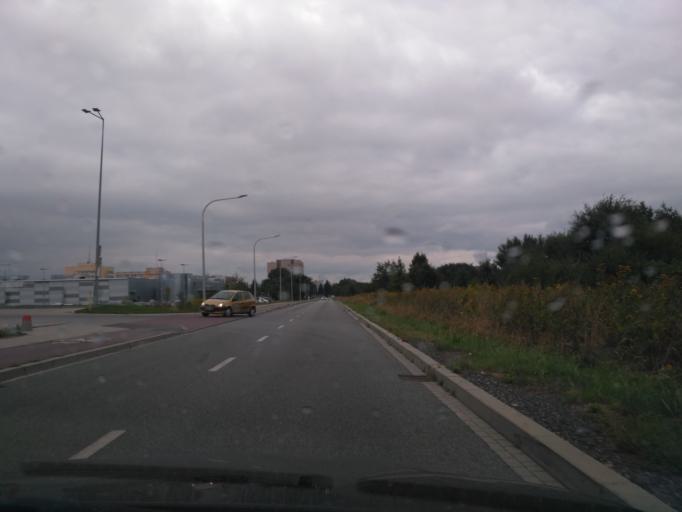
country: PL
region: Subcarpathian Voivodeship
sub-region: Krosno
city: Krosno
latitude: 49.6756
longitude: 21.7794
